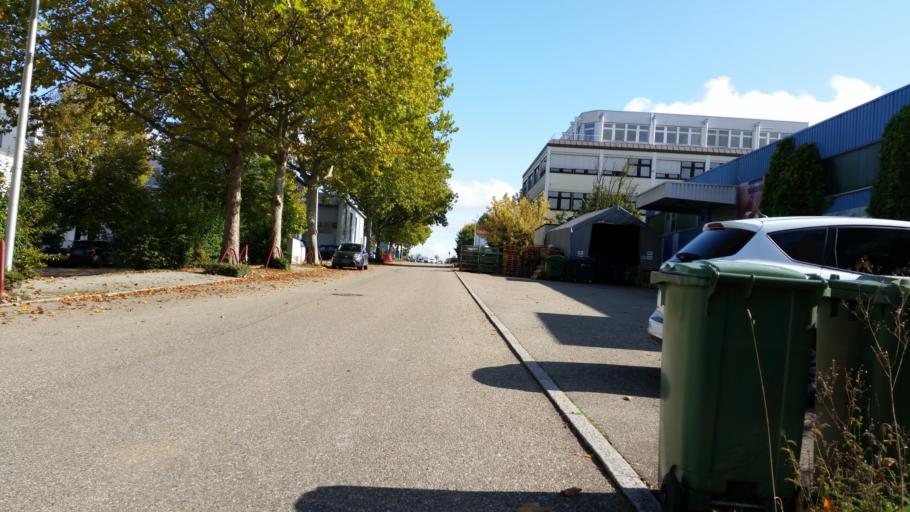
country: DE
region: Baden-Wuerttemberg
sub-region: Regierungsbezirk Stuttgart
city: Freiberg am Neckar
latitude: 48.9296
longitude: 9.2037
